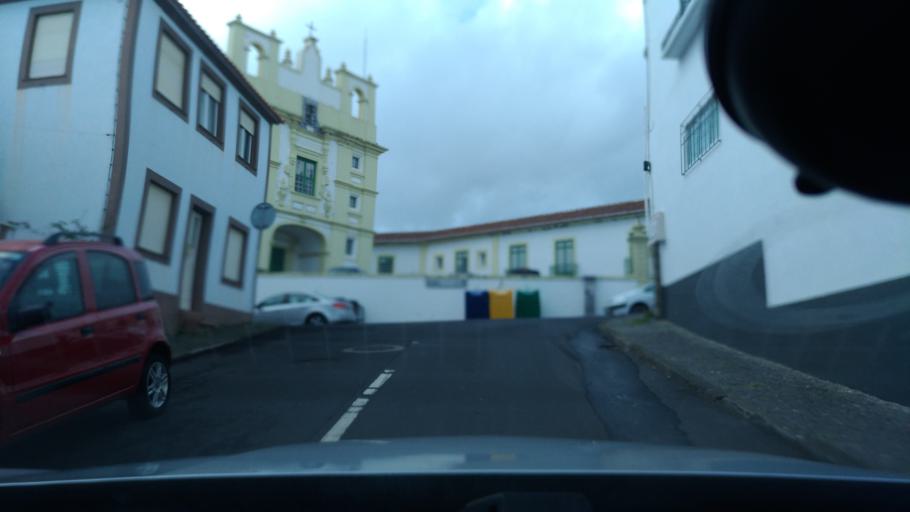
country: PT
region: Azores
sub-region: Angra do Heroismo
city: Angra do Heroismo
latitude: 38.6547
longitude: -27.2152
